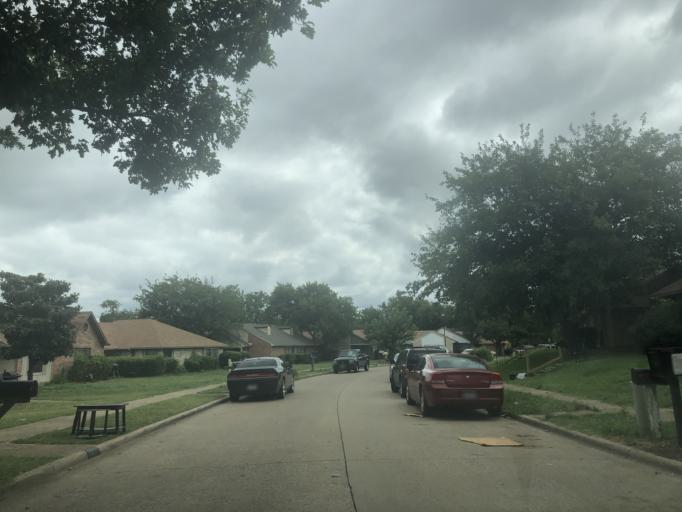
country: US
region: Texas
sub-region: Dallas County
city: Duncanville
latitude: 32.6366
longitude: -96.9454
